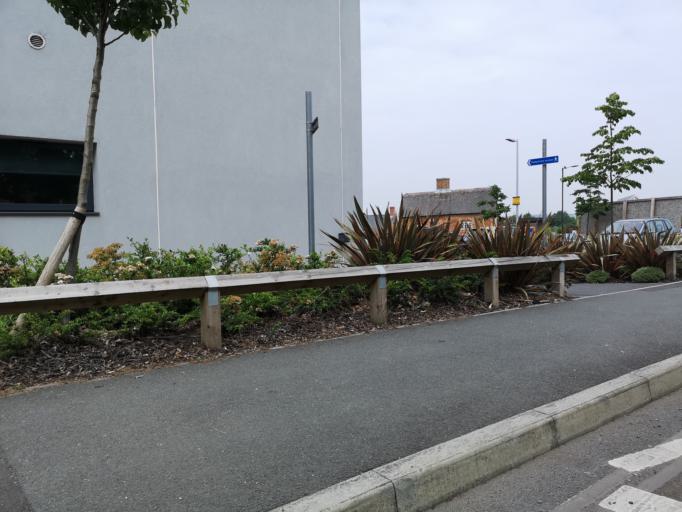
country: GB
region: England
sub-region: Isle of Wight
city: Sandown
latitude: 50.6455
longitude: -1.1790
